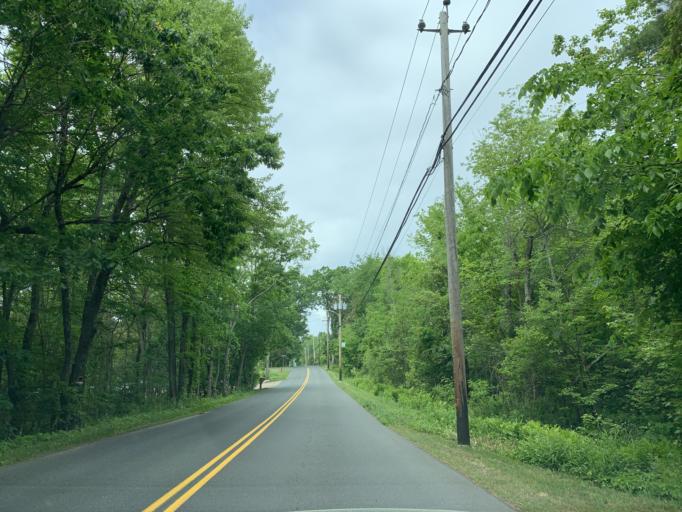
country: US
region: Massachusetts
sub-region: Hampshire County
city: Southampton
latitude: 42.1837
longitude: -72.7307
